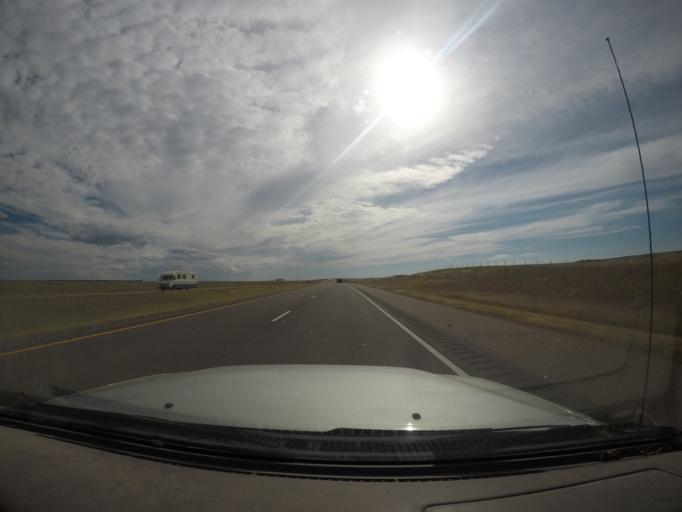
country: US
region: Nebraska
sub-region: Kimball County
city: Kimball
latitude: 41.2127
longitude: -103.6935
